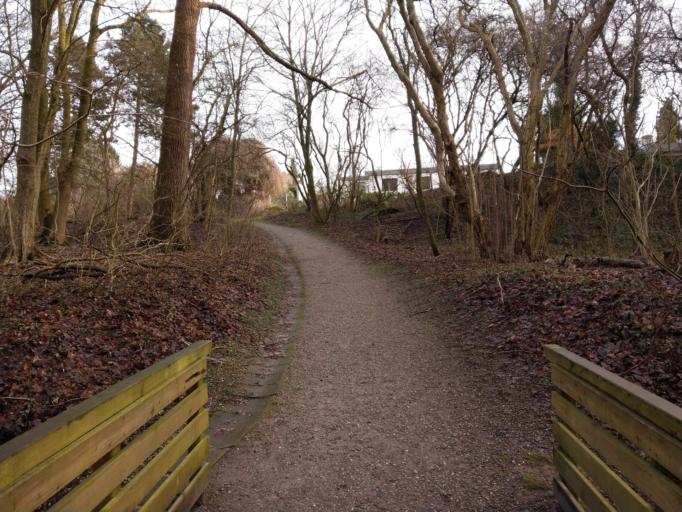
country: DE
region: Schleswig-Holstein
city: Flensburg
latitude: 54.8040
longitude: 9.4528
